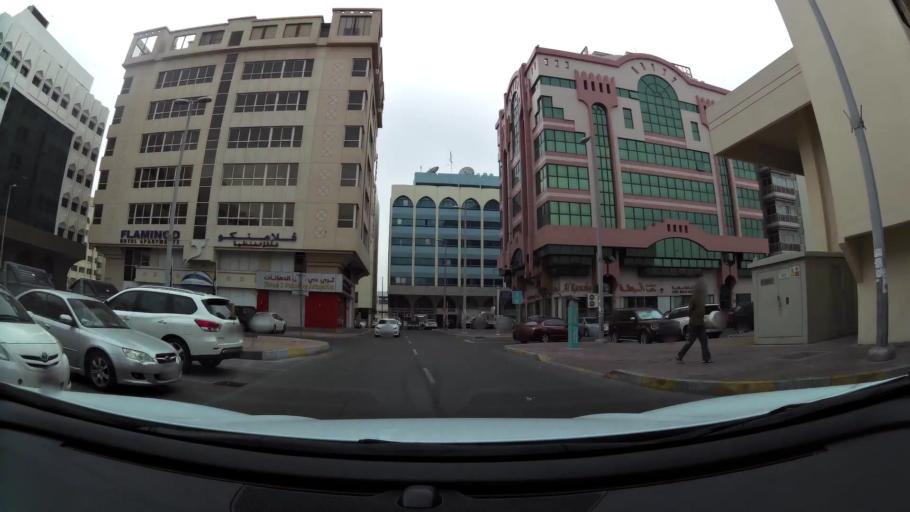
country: AE
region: Abu Dhabi
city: Abu Dhabi
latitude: 24.4801
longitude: 54.3665
